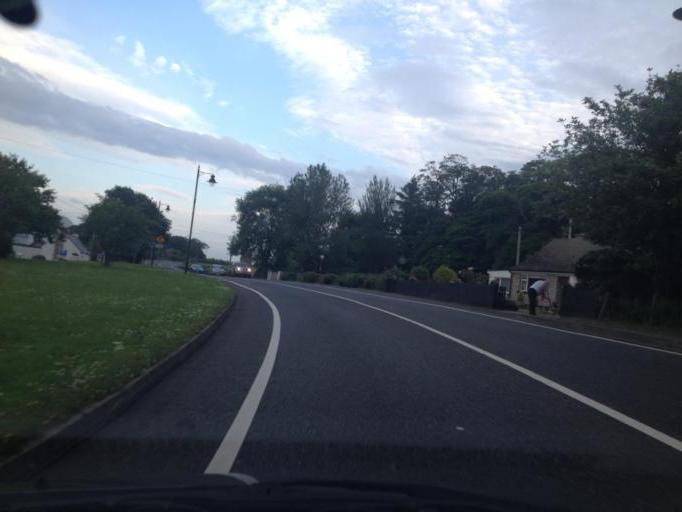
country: IE
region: Connaught
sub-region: Sligo
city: Sligo
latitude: 54.3276
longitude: -8.4999
